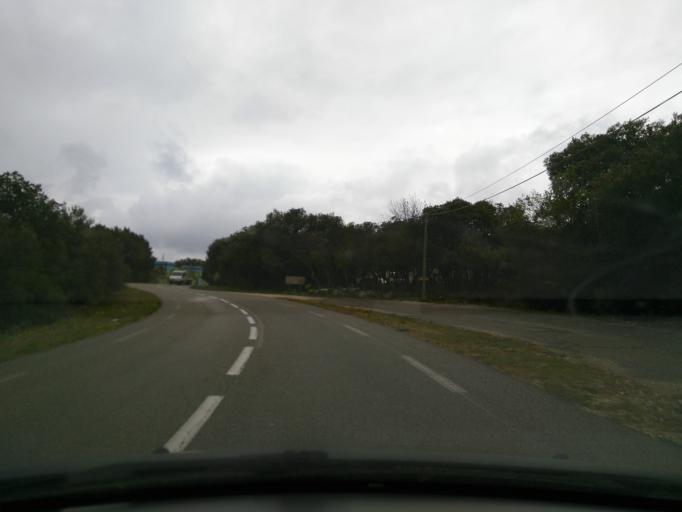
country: FR
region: Languedoc-Roussillon
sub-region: Departement du Gard
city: Barjac
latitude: 44.3263
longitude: 4.4174
